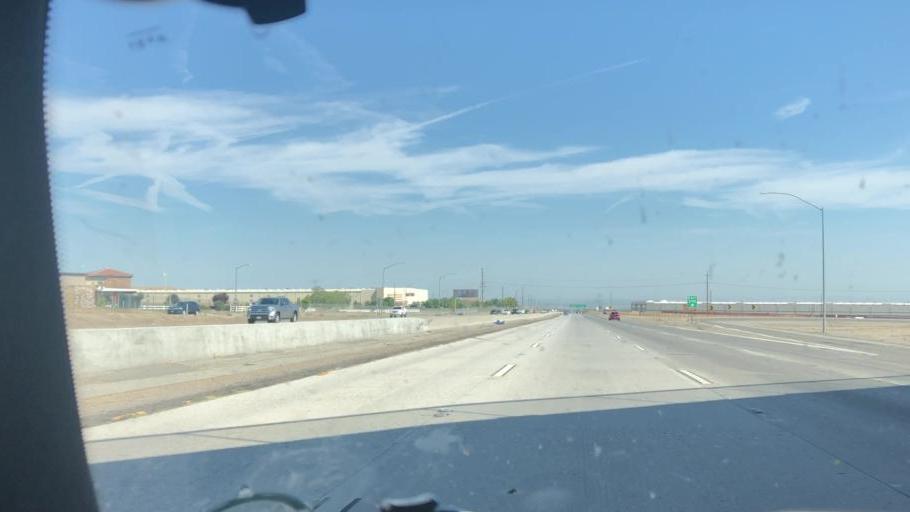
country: US
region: California
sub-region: Kern County
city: Frazier Park
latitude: 34.9866
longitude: -118.9453
